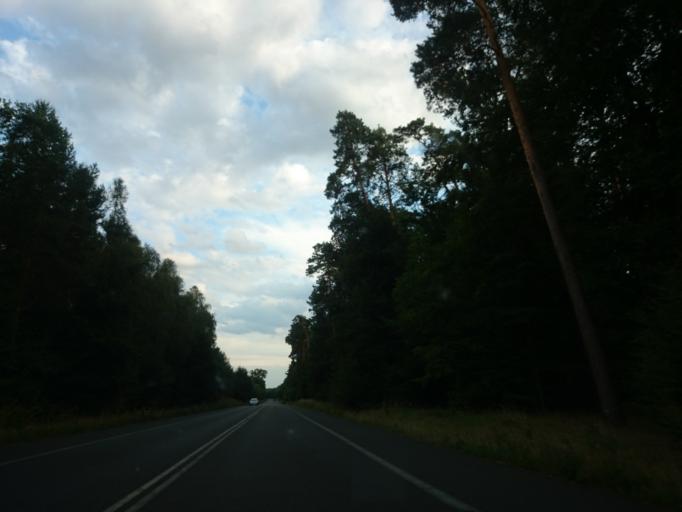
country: PL
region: Lubusz
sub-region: Powiat gorzowski
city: Jenin
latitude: 52.7997
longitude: 15.1029
